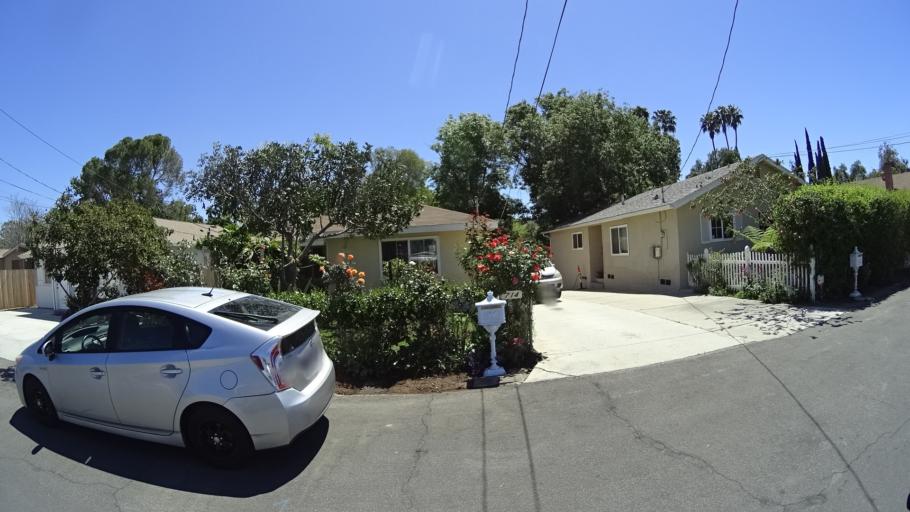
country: US
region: California
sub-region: Ventura County
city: Thousand Oaks
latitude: 34.1835
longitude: -118.8651
